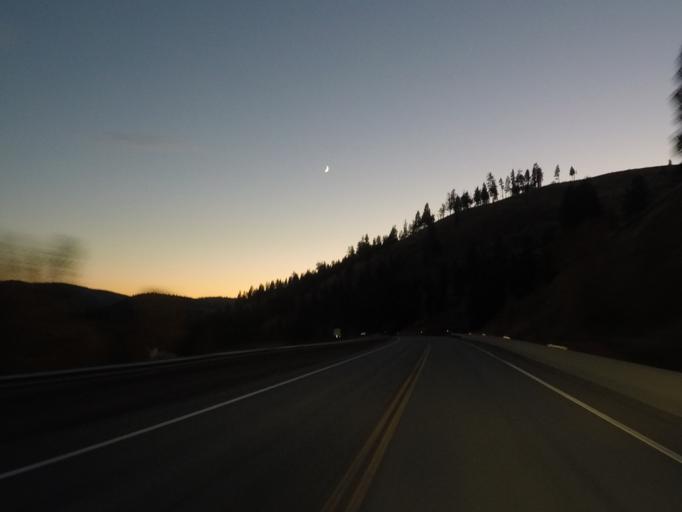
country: US
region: Montana
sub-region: Missoula County
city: Seeley Lake
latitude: 47.0227
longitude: -113.3157
